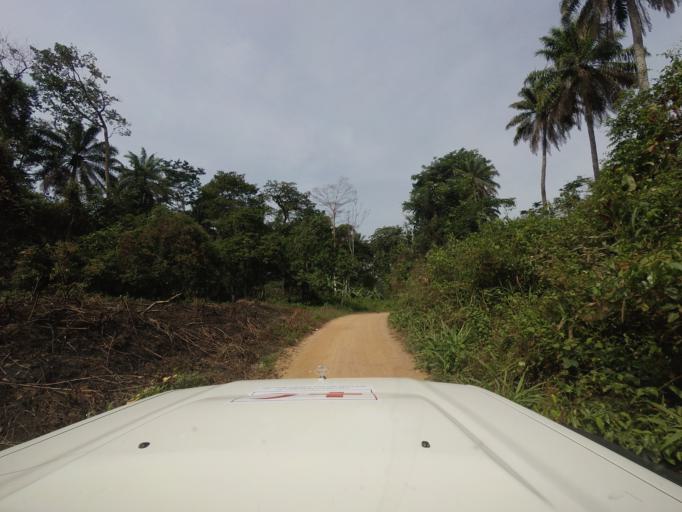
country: GN
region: Nzerekore
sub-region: Macenta
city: Macenta
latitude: 8.4685
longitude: -9.5732
